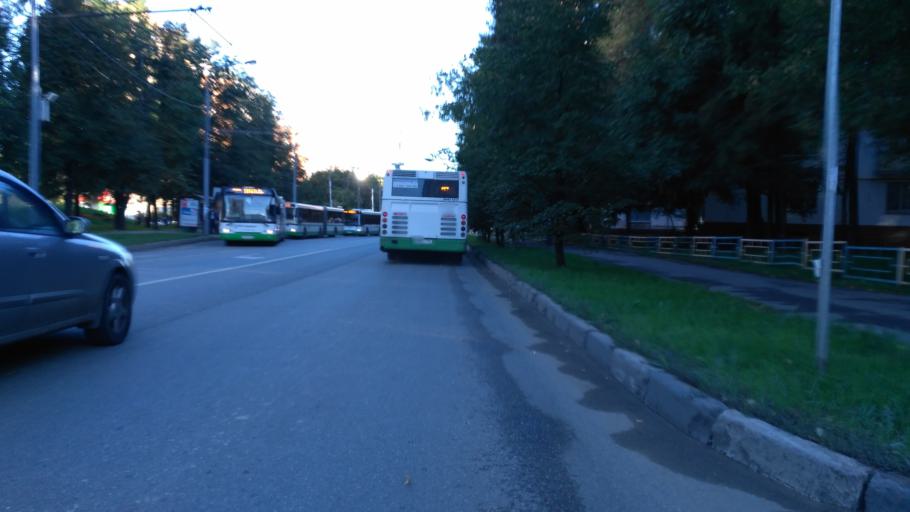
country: RU
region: Moscow
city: Likhobory
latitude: 55.8630
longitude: 37.5614
